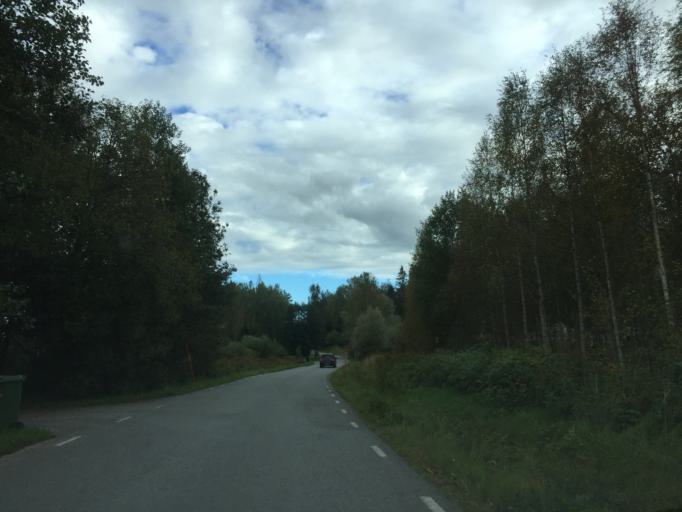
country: SE
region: OErebro
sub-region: Orebro Kommun
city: Hovsta
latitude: 59.3257
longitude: 15.1884
